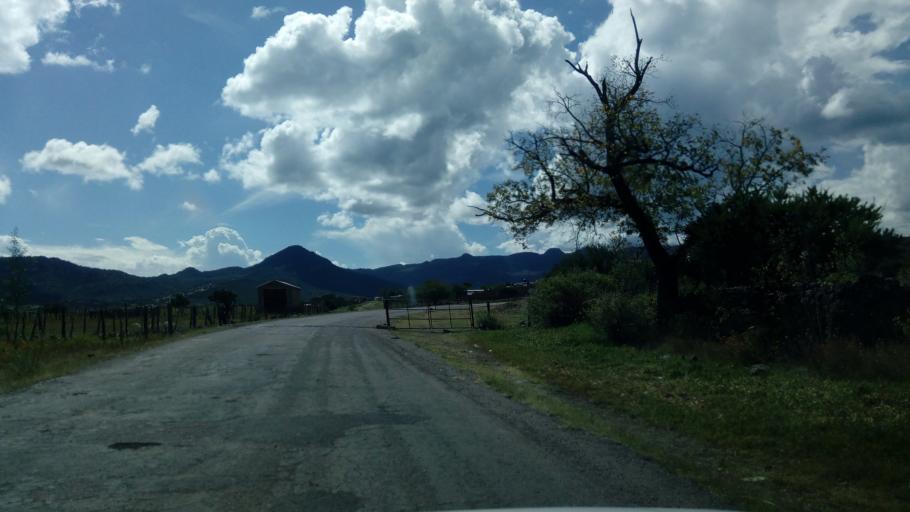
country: MX
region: Durango
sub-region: Durango
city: Jose Refugio Salcido
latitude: 23.7963
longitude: -104.4860
